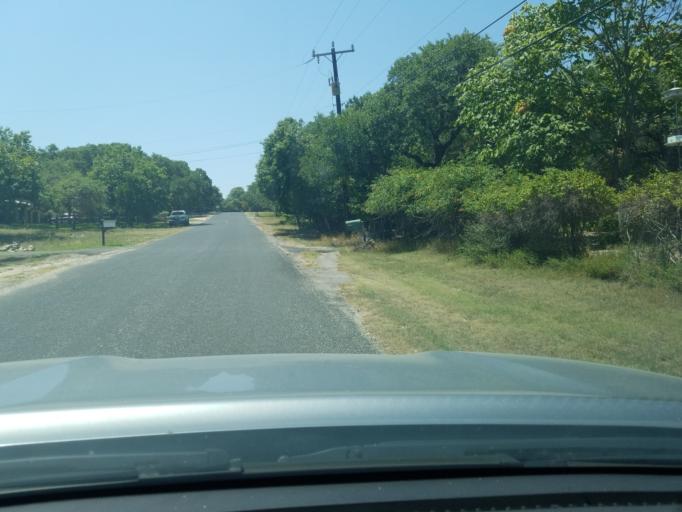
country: US
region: Texas
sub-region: Bexar County
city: Timberwood Park
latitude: 29.7112
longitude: -98.4923
